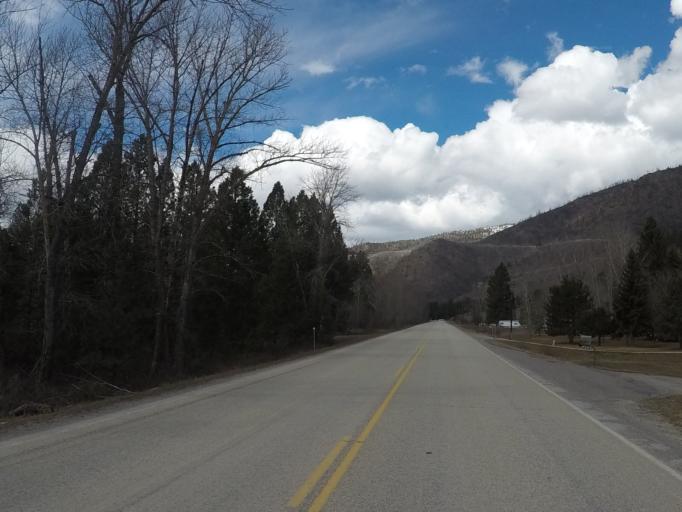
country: US
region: Montana
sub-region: Missoula County
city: Lolo
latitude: 46.7488
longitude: -114.1991
